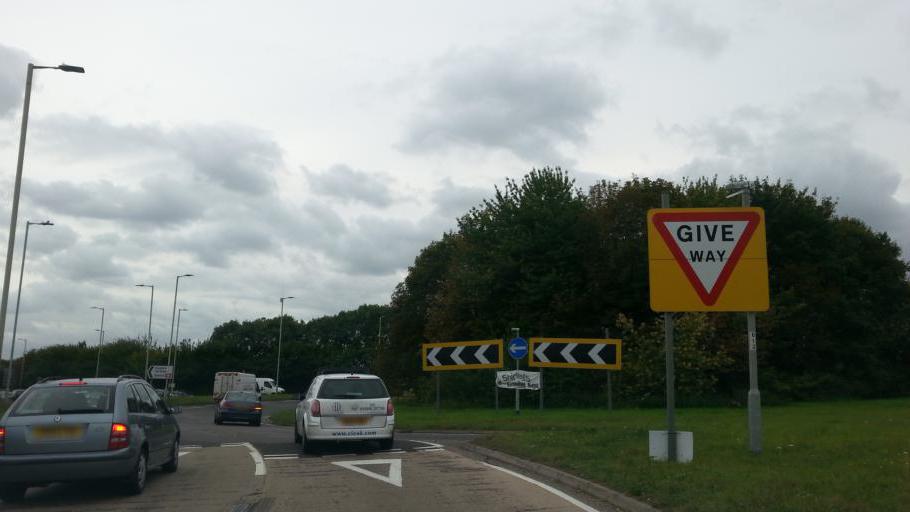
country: GB
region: England
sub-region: Hertfordshire
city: Royston
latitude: 52.0617
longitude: -0.0289
